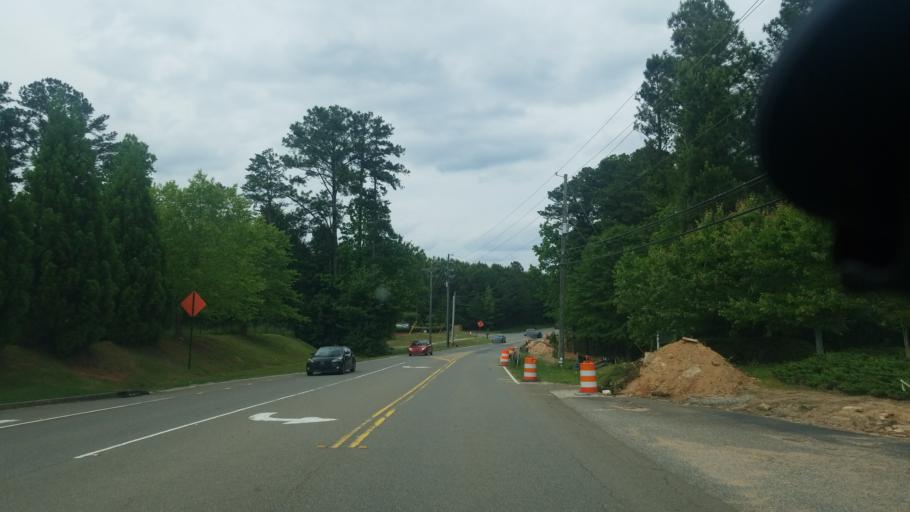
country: US
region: Georgia
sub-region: Forsyth County
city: Cumming
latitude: 34.1844
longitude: -84.1234
